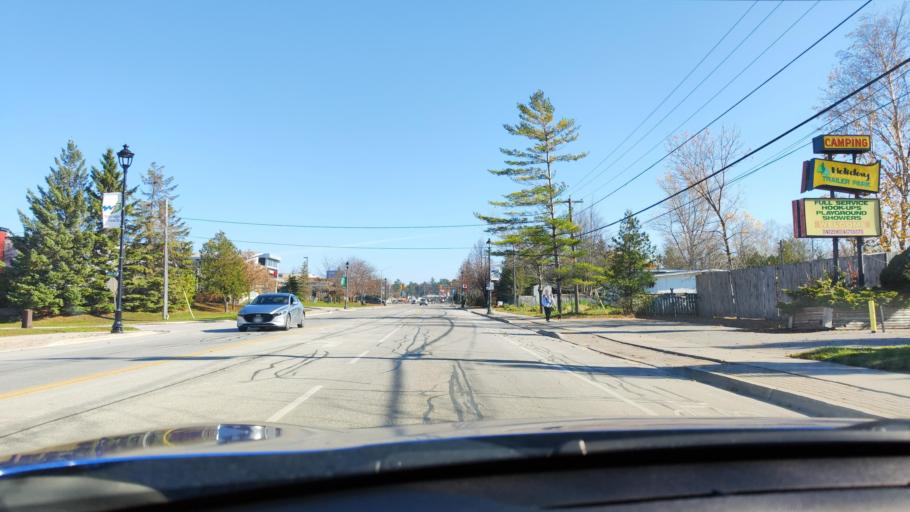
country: CA
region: Ontario
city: Wasaga Beach
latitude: 44.5230
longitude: -80.0103
